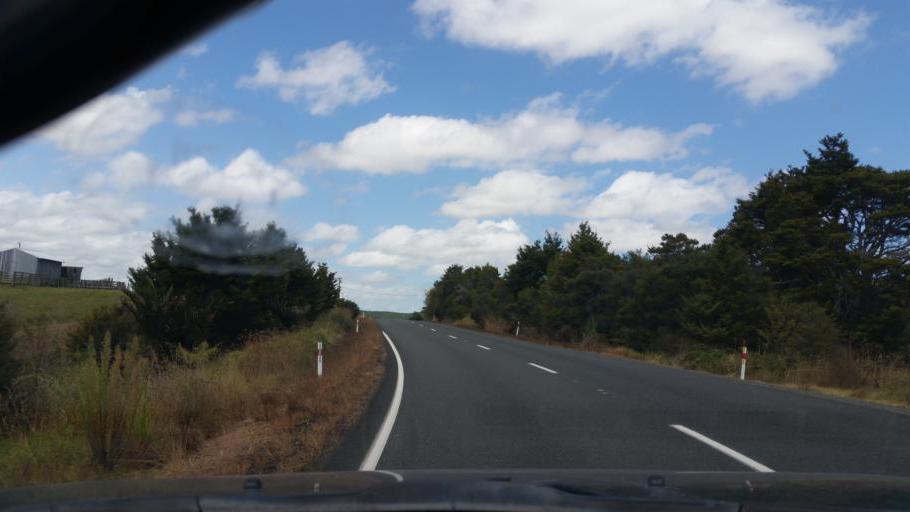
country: NZ
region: Northland
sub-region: Kaipara District
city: Dargaville
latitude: -35.8705
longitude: 173.8425
